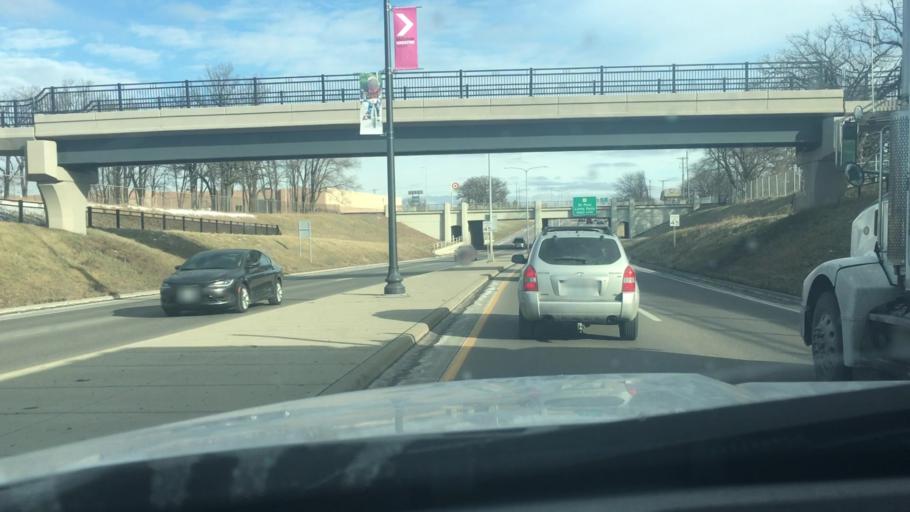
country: US
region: Minnesota
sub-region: Stearns County
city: Saint Cloud
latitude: 45.5631
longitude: -94.1474
